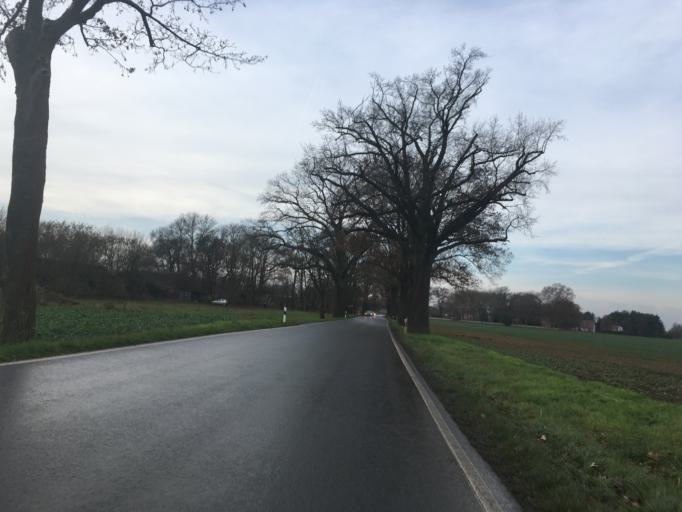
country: DE
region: Brandenburg
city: Letschin
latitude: 52.7031
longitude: 14.3671
